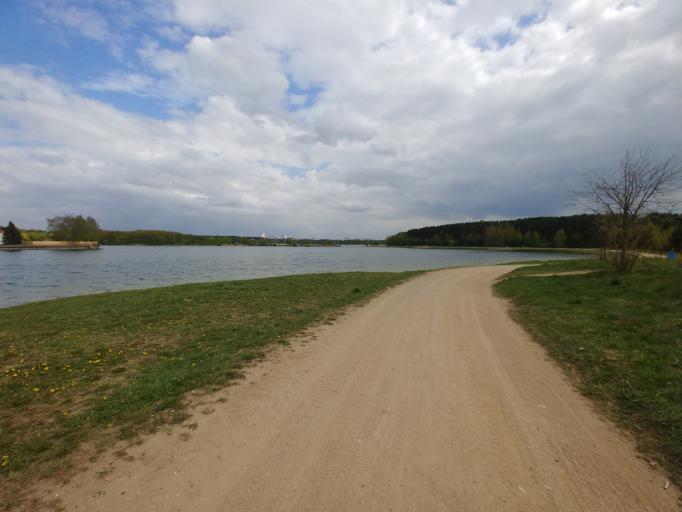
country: BY
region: Minsk
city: Bal'shavik
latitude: 53.9595
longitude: 27.5710
